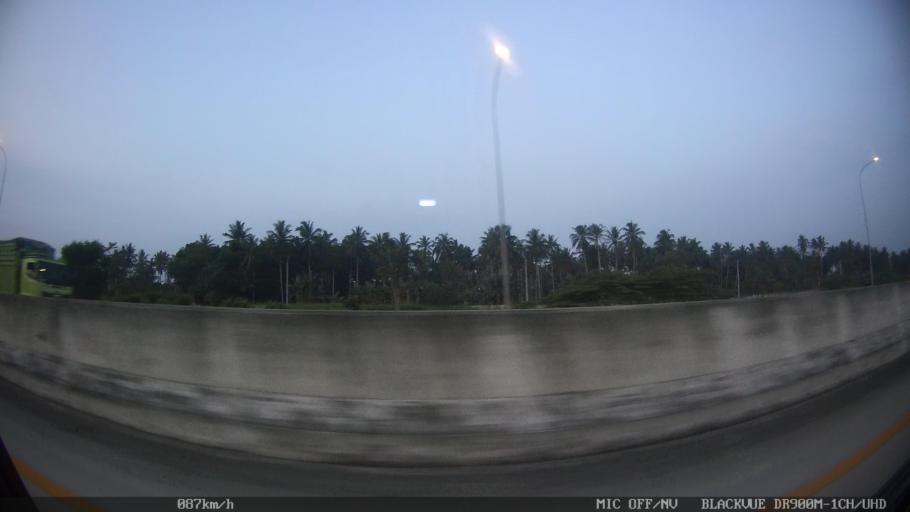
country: ID
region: Lampung
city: Sidorejo
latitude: -5.6502
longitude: 105.5821
